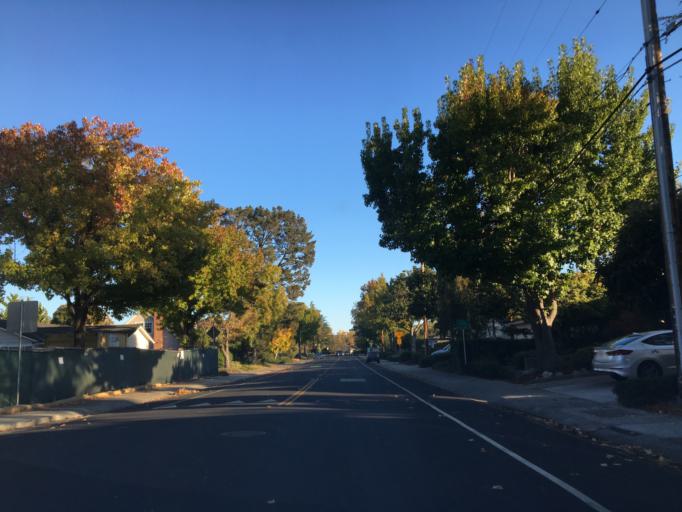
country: US
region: California
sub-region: Santa Clara County
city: Palo Alto
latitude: 37.4256
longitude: -122.1232
